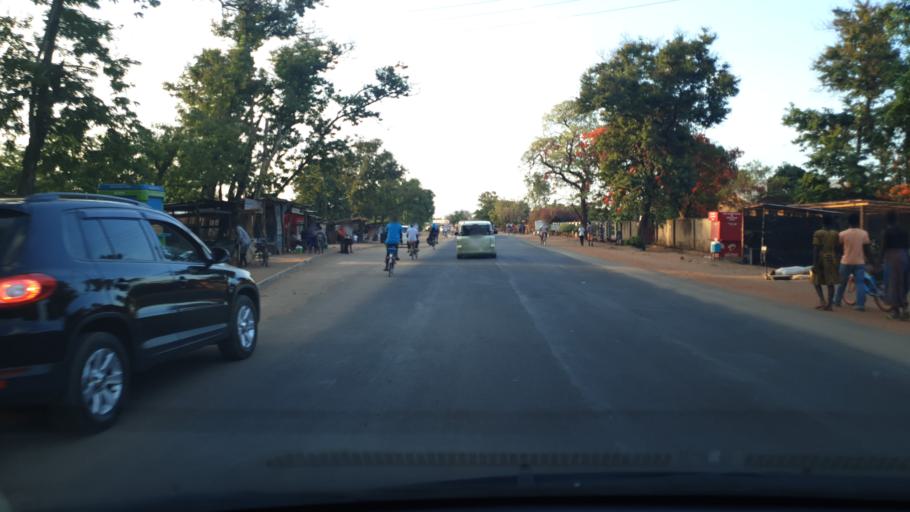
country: MW
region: Central Region
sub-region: Salima District
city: Salima
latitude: -13.7744
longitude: 34.4499
